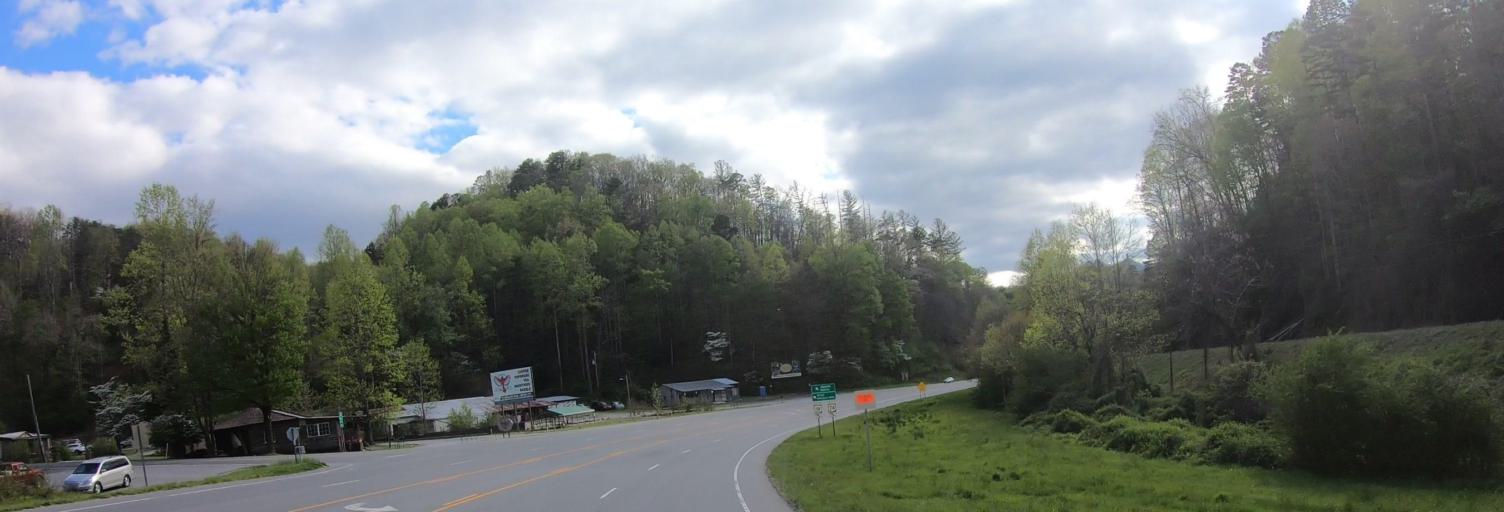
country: US
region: North Carolina
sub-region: Swain County
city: Bryson City
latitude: 35.3663
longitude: -83.5492
